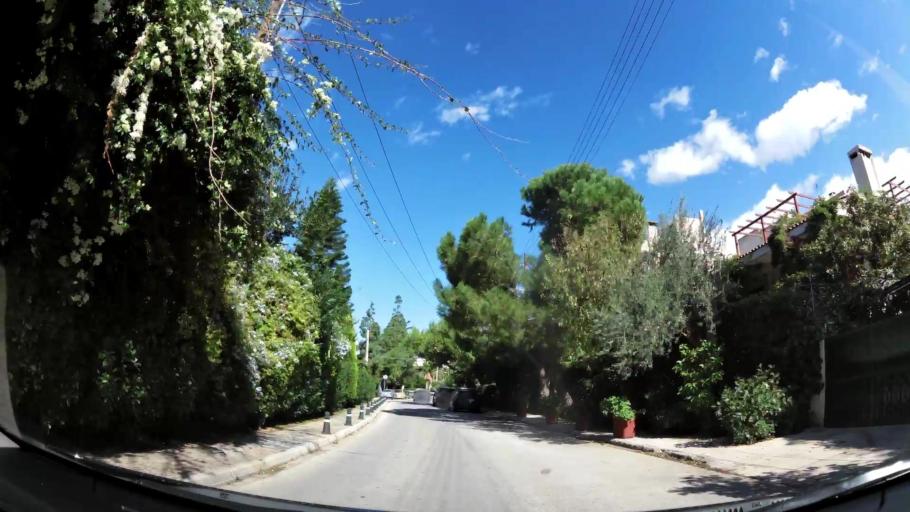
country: GR
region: Attica
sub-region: Nomarchia Anatolikis Attikis
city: Voula
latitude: 37.8287
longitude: 23.7788
